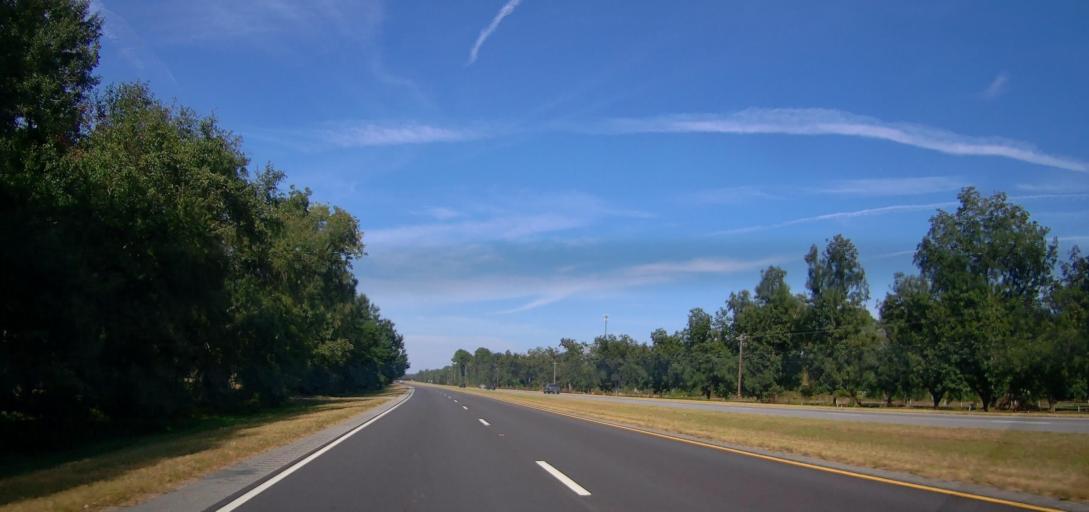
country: US
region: Georgia
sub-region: Dougherty County
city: Putney
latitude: 31.3894
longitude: -84.1476
